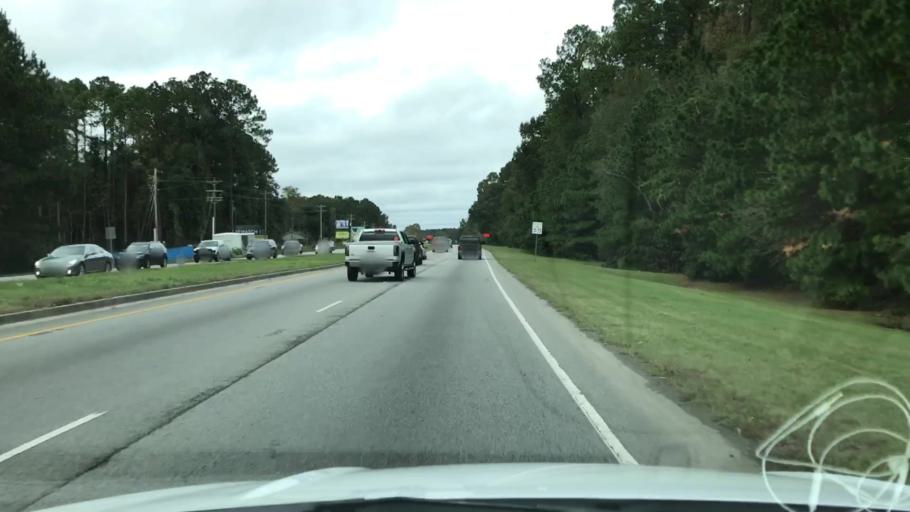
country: US
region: South Carolina
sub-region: Beaufort County
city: Bluffton
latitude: 32.3127
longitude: -80.9346
